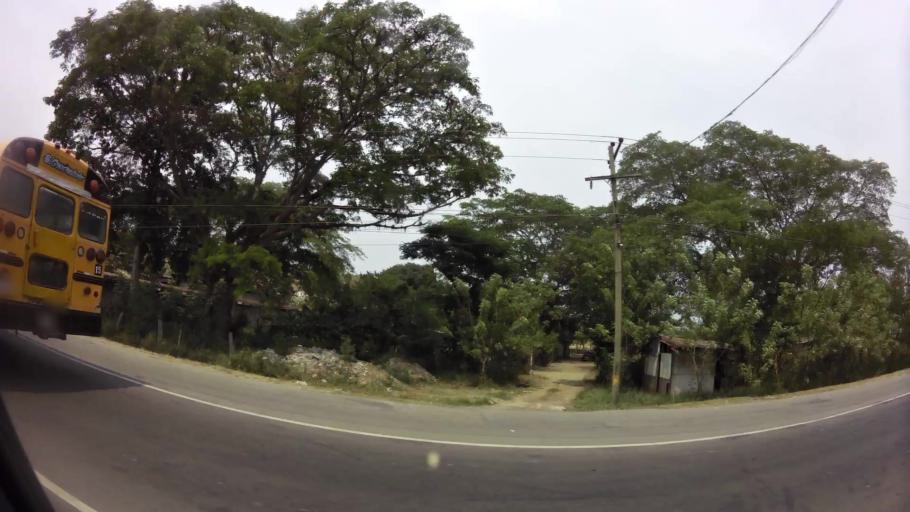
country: HN
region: Cortes
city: Nuevo Chamelecon
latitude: 15.3781
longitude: -87.9885
